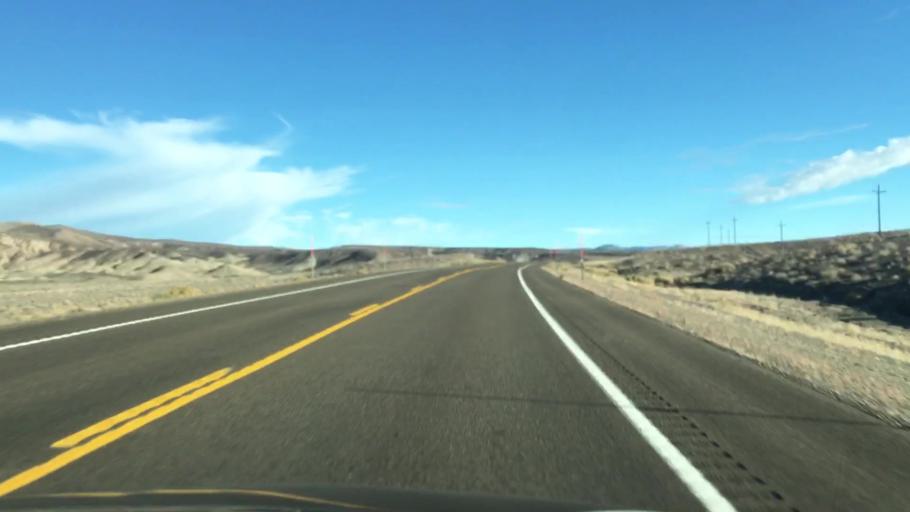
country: US
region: Nevada
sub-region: Mineral County
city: Hawthorne
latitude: 38.2362
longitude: -118.0281
